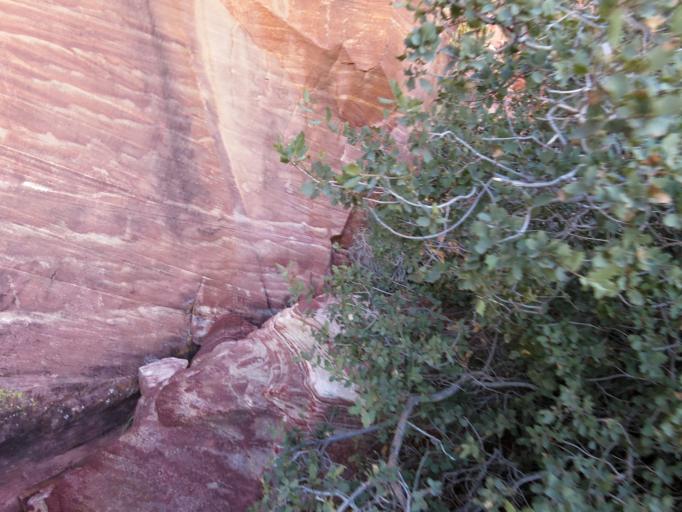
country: US
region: Nevada
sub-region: Clark County
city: Summerlin South
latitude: 36.1495
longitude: -115.4267
